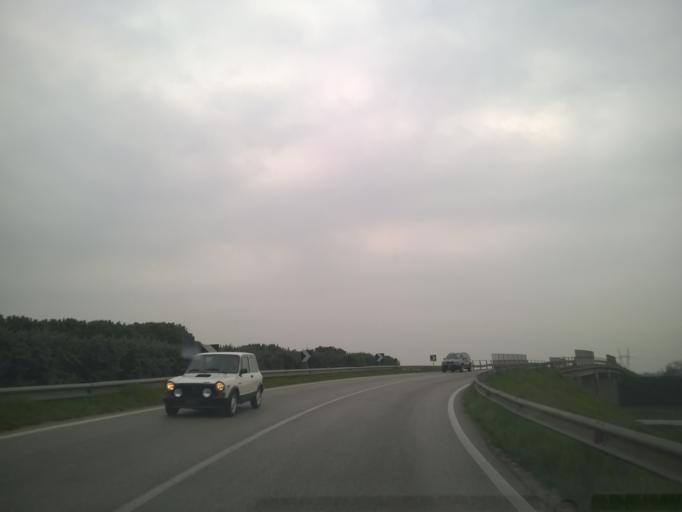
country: IT
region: Veneto
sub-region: Provincia di Padova
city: Carmignano di Brenta
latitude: 45.6170
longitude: 11.7009
